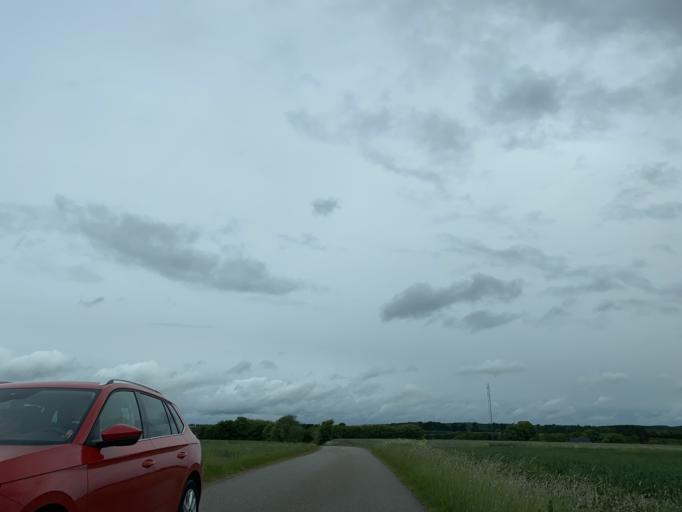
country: DK
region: Central Jutland
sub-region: Favrskov Kommune
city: Hammel
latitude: 56.2398
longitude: 9.7959
